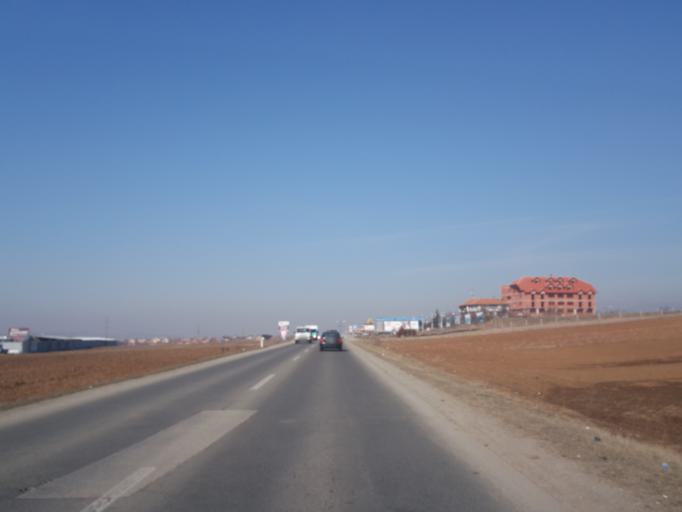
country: XK
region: Mitrovica
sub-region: Vushtrri
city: Vushtrri
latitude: 42.7726
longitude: 21.0188
